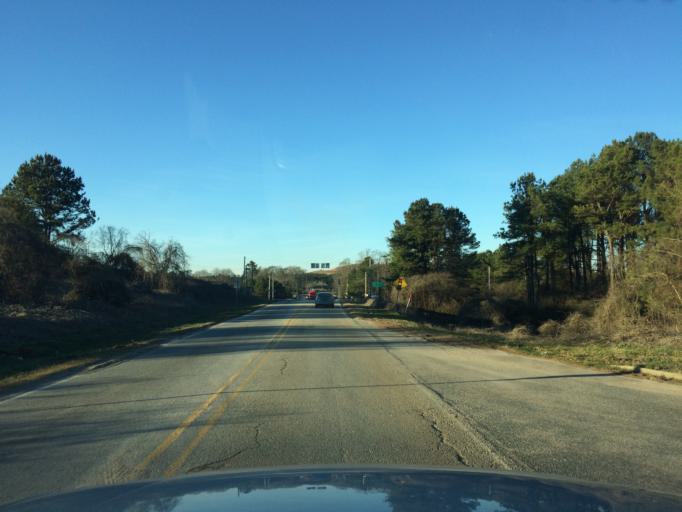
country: US
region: Georgia
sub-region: Barrow County
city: Winder
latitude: 33.9511
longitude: -83.7677
